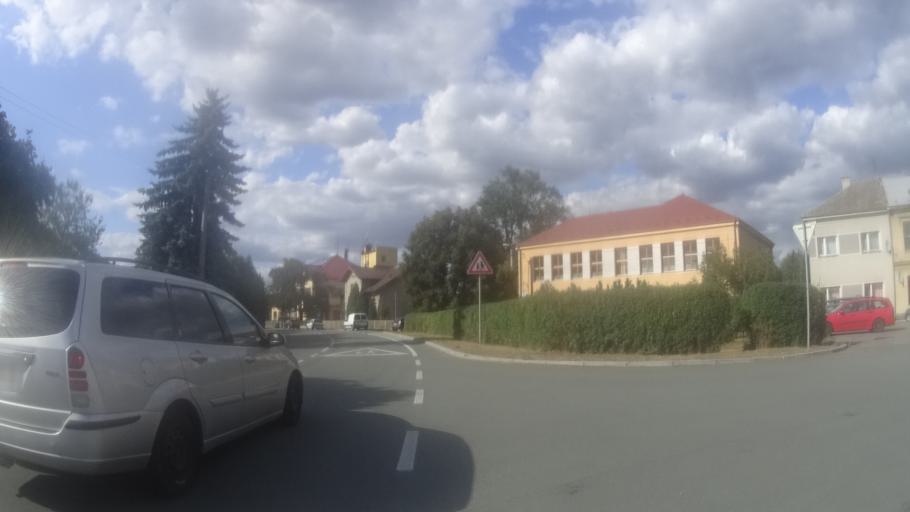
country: CZ
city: Albrechtice nad Orlici
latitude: 50.1402
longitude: 16.0635
